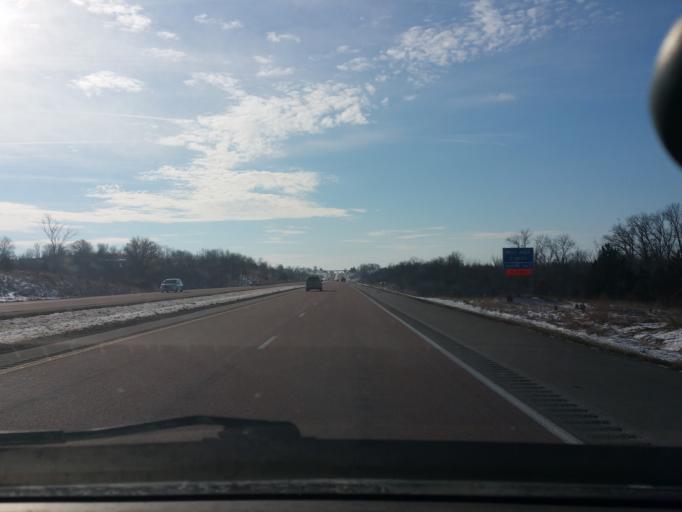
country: US
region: Iowa
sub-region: Warren County
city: Norwalk
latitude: 41.3093
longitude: -93.7787
